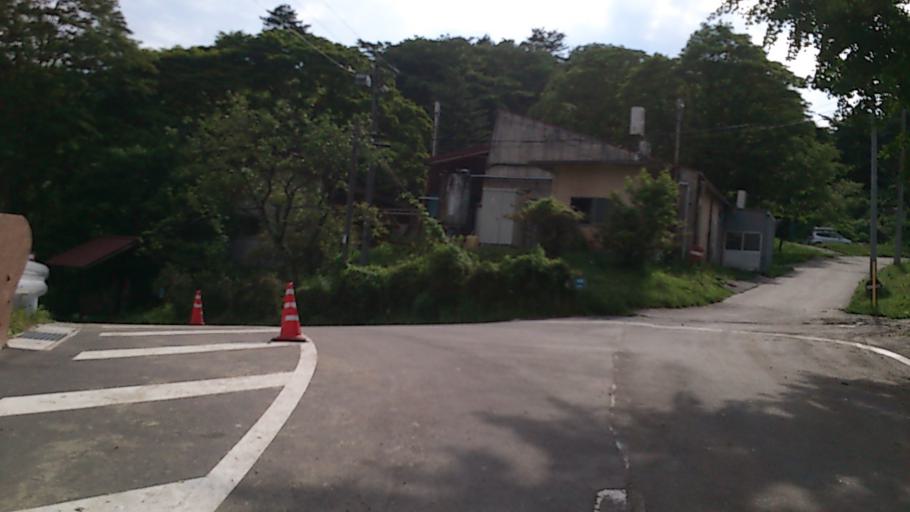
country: JP
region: Nagano
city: Saku
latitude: 36.2494
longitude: 138.6214
